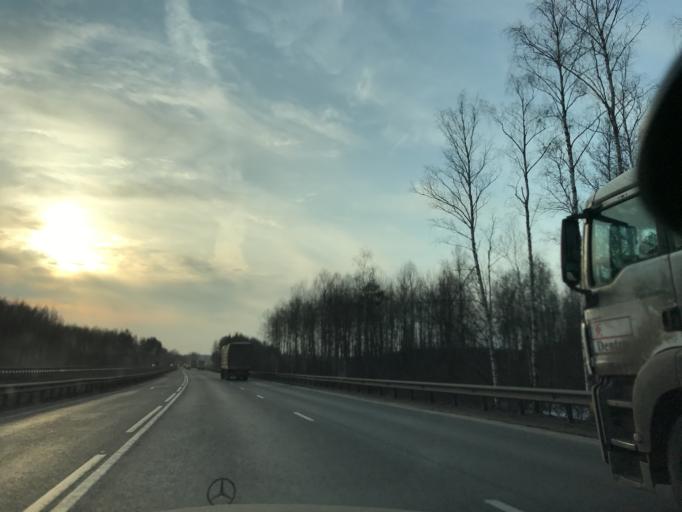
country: RU
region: Vladimir
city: Kosterevo
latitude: 55.9584
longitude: 39.6590
